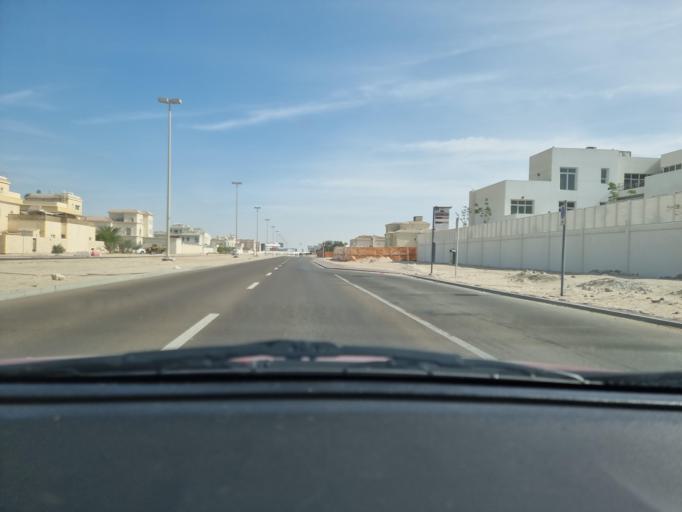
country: AE
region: Abu Dhabi
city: Abu Dhabi
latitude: 24.3154
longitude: 54.5455
